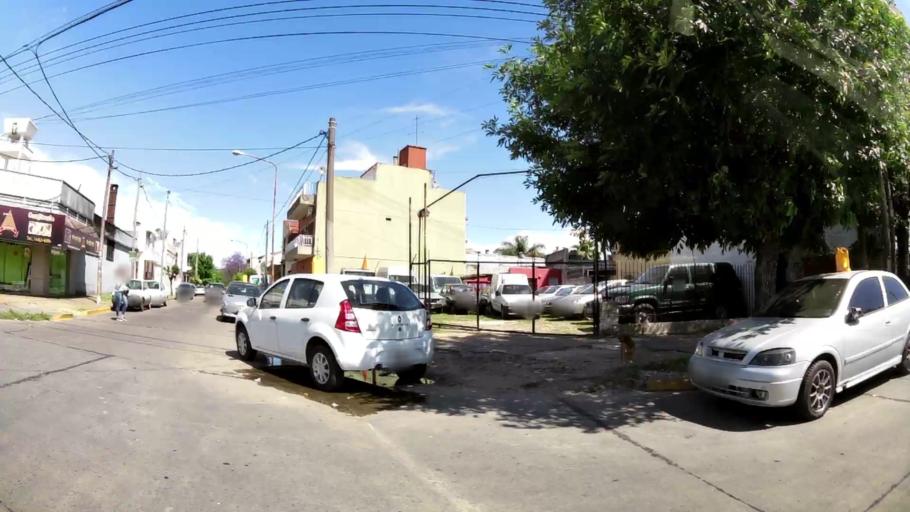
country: AR
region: Buenos Aires
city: San Justo
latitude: -34.6659
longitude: -58.5462
